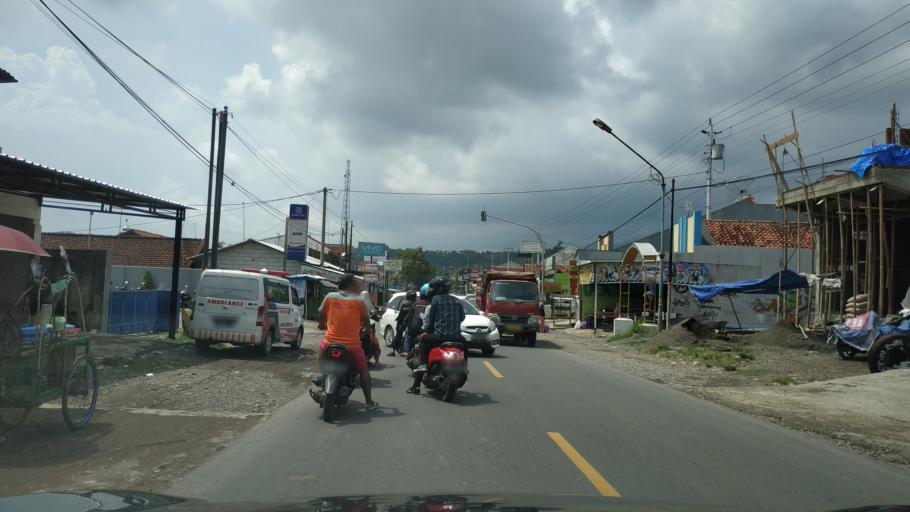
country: ID
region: Central Java
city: Lebaksiu
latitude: -7.0465
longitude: 109.1422
